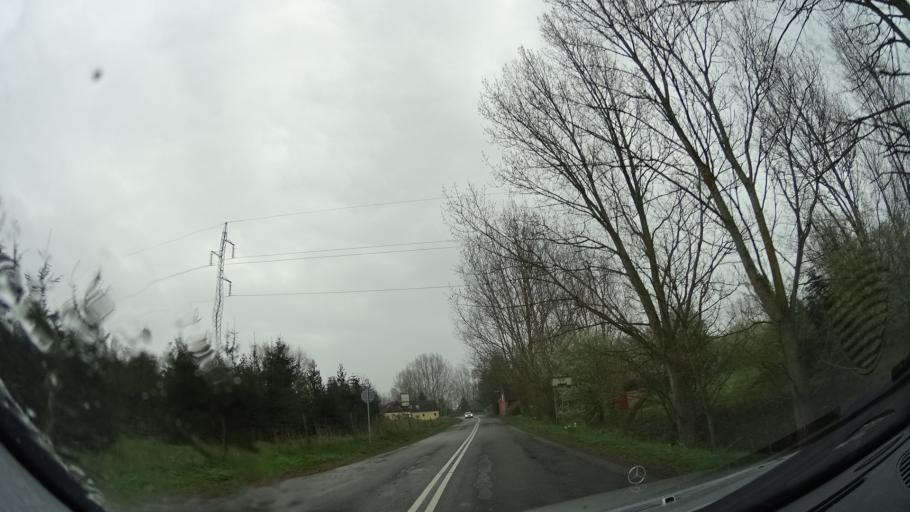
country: DK
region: Zealand
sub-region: Odsherred Kommune
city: Hojby
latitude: 55.8543
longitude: 11.5632
